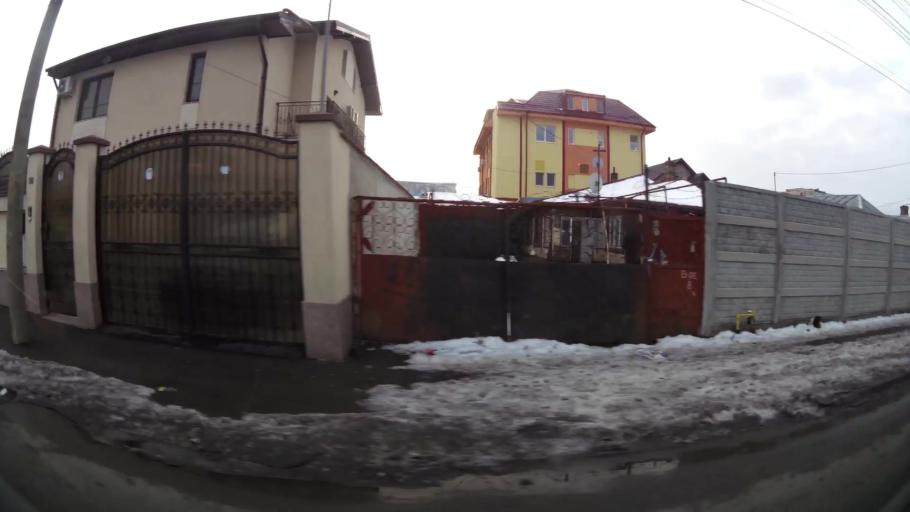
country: RO
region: Ilfov
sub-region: Comuna Fundeni-Dobroesti
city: Fundeni
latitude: 44.4741
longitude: 26.1605
